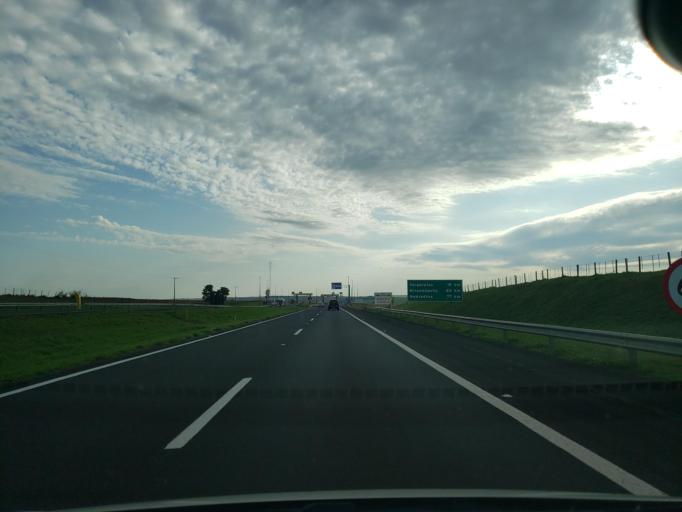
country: BR
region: Sao Paulo
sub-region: Guararapes
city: Guararapes
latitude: -21.2106
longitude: -50.7284
